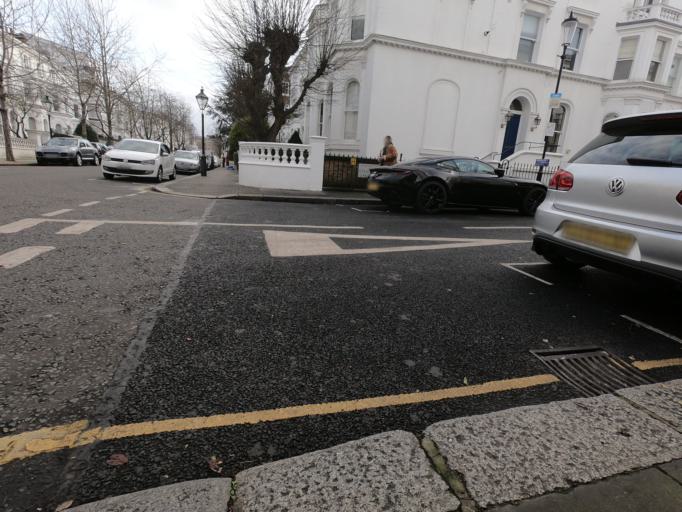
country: GB
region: England
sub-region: Greater London
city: Kensington
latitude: 51.5079
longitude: -0.1929
